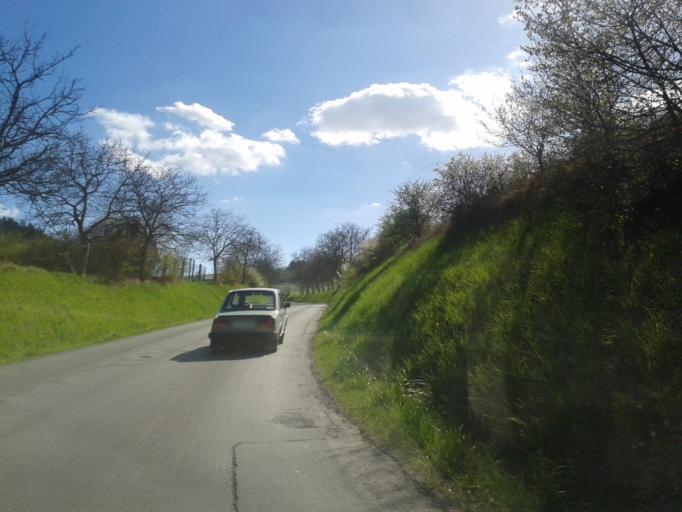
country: CZ
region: Central Bohemia
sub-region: Okres Beroun
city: Beroun
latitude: 49.9466
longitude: 14.0706
